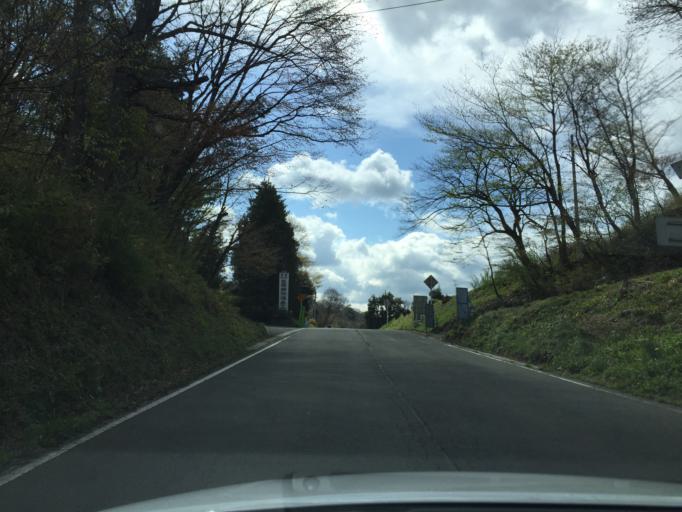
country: JP
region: Fukushima
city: Funehikimachi-funehiki
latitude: 37.6192
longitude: 140.6481
